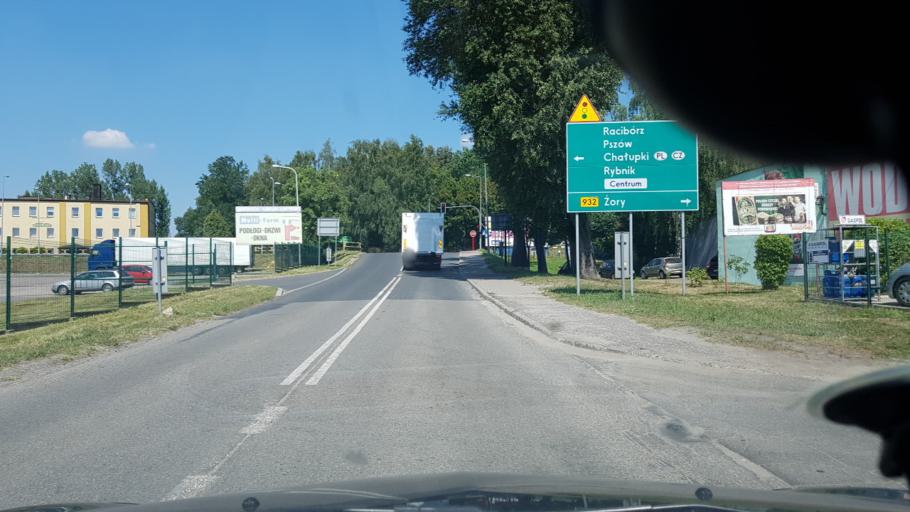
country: PL
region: Silesian Voivodeship
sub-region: Powiat wodzislawski
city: Wodzislaw Slaski
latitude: 50.0118
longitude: 18.4811
